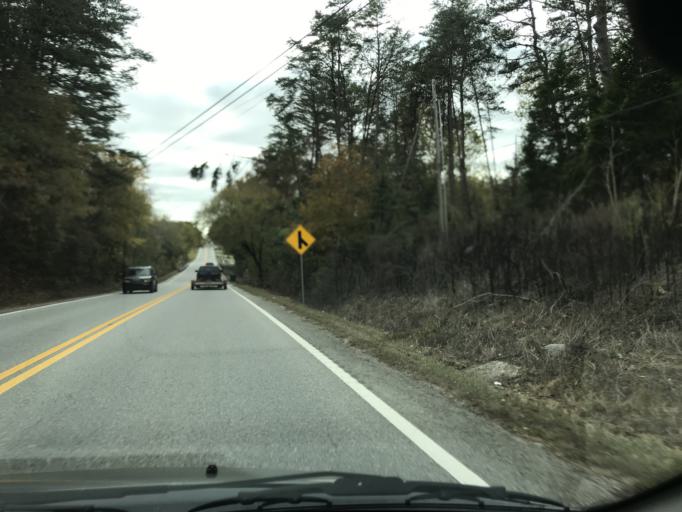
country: US
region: Tennessee
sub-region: Hamilton County
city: Lakesite
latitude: 35.2289
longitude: -85.0204
